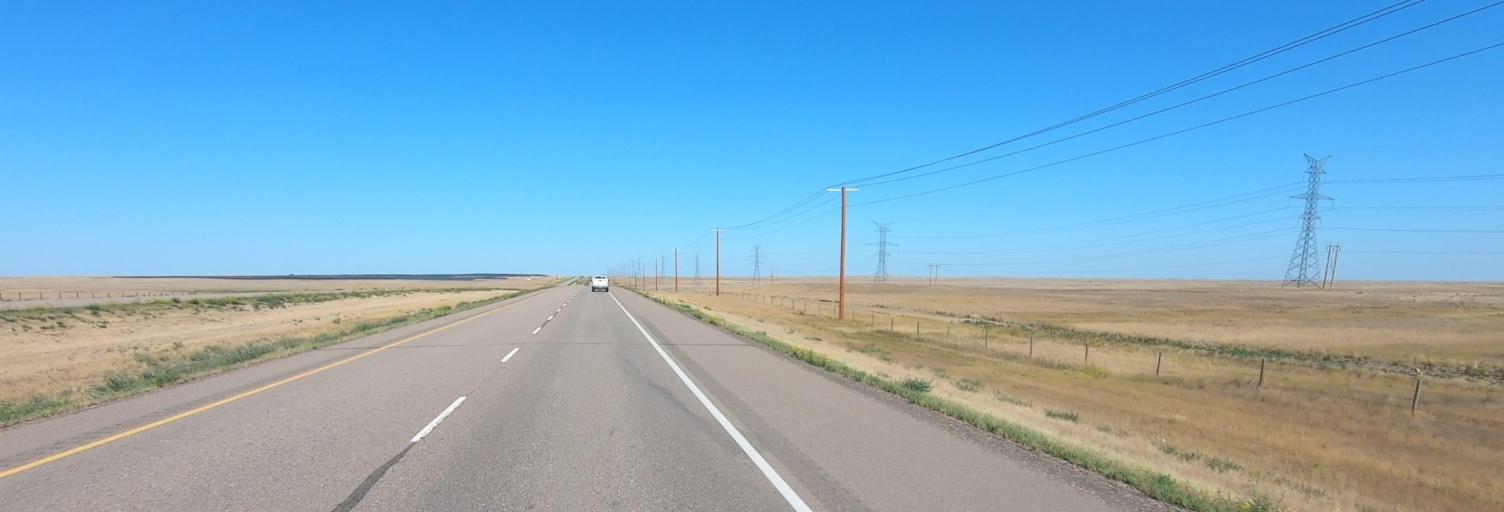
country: CA
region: Alberta
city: Bow Island
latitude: 50.2618
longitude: -111.2492
